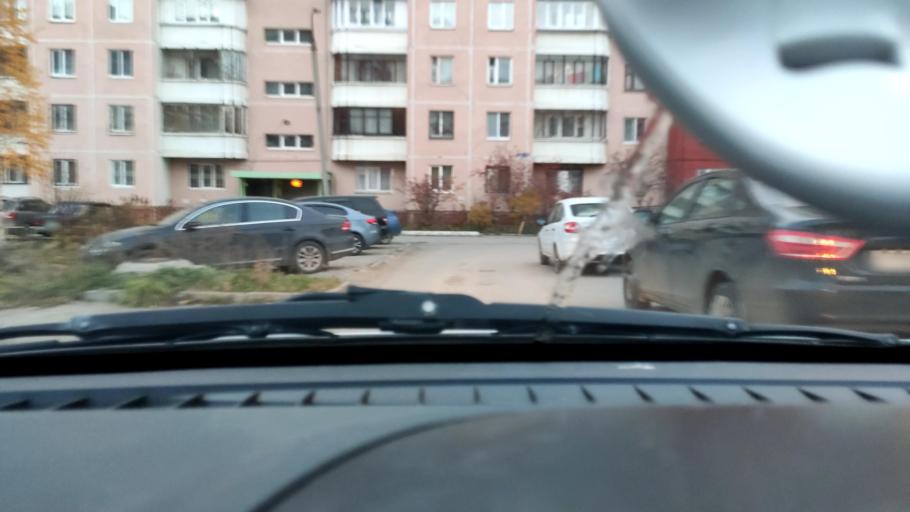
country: RU
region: Perm
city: Kondratovo
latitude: 57.9941
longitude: 56.1351
